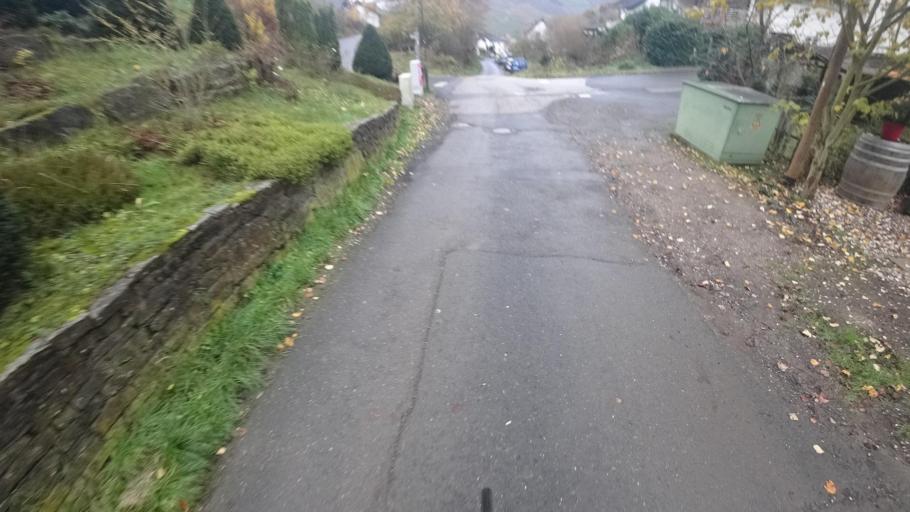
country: DE
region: Rheinland-Pfalz
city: Rech
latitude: 50.5108
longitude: 7.0409
